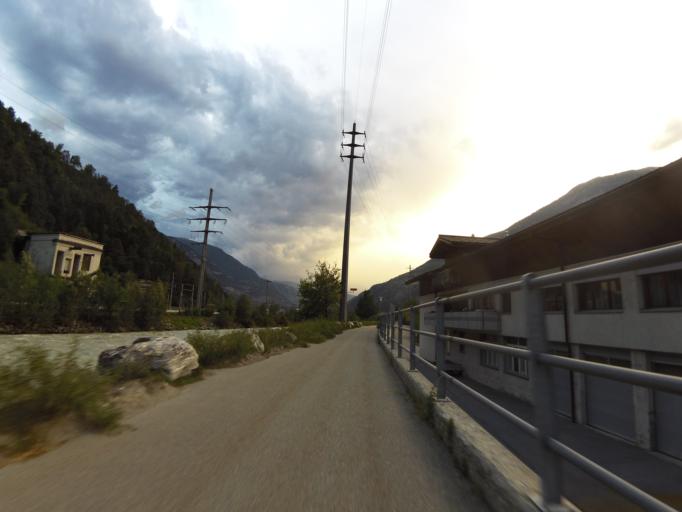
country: CH
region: Valais
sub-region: Brig District
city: Naters
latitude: 46.3259
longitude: 8.0084
